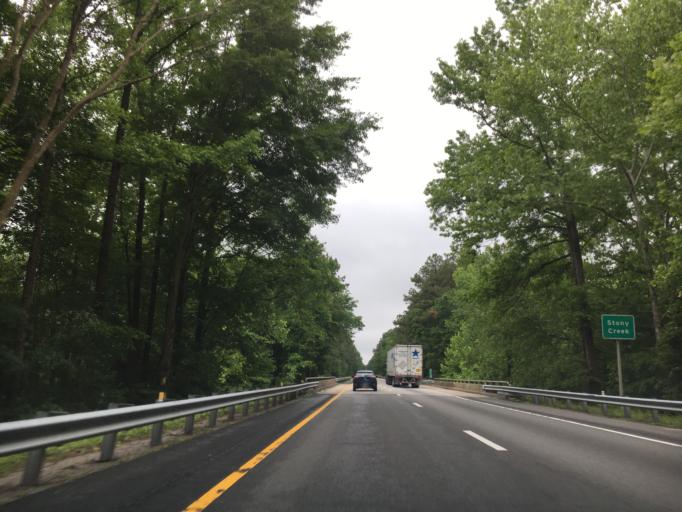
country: US
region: Virginia
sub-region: Dinwiddie County
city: Dinwiddie
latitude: 37.0618
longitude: -77.5932
